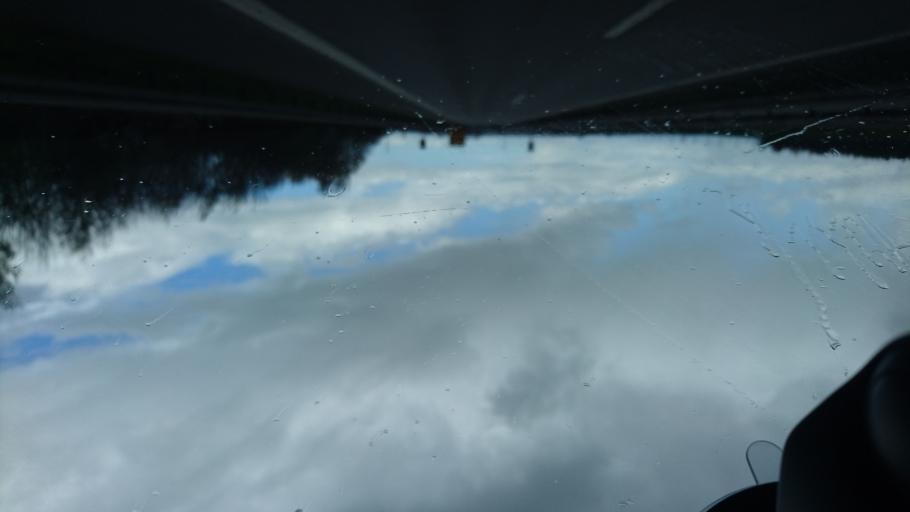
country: DE
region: Mecklenburg-Vorpommern
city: Kritzmow
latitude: 54.0383
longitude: 12.0489
